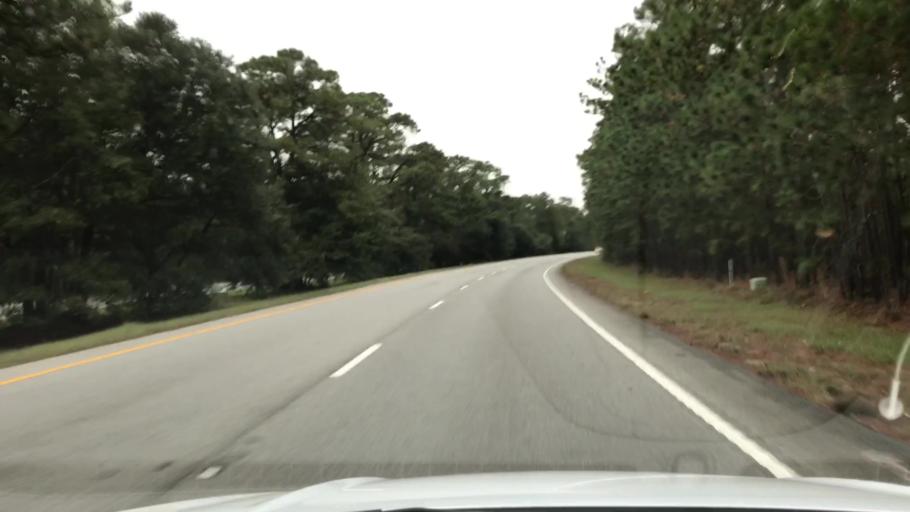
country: US
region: South Carolina
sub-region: Georgetown County
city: Georgetown
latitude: 33.4037
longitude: -79.1992
